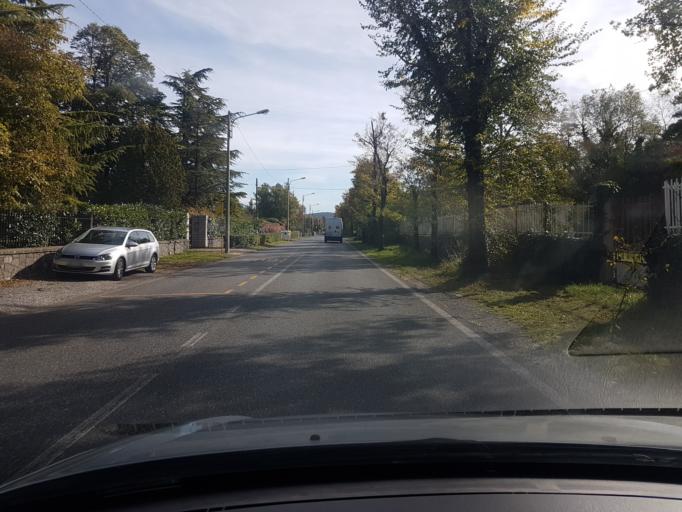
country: IT
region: Friuli Venezia Giulia
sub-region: Provincia di Trieste
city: Prosecco-Contovello
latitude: 45.7185
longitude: 13.7232
